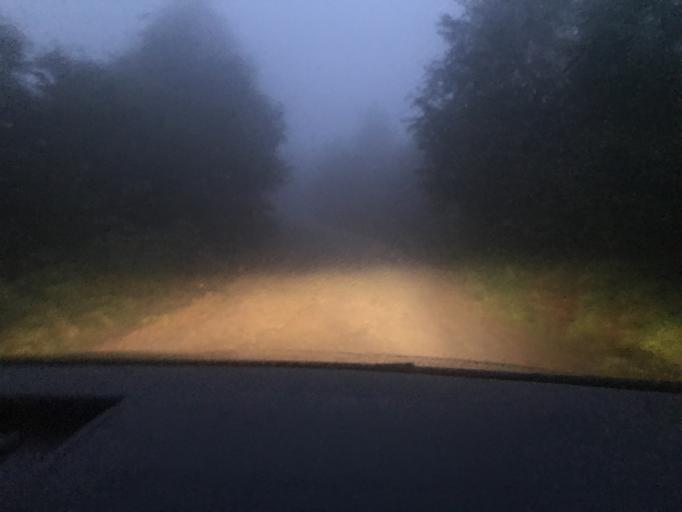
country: TR
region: Trabzon
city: Hayrat
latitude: 40.8230
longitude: 40.3875
